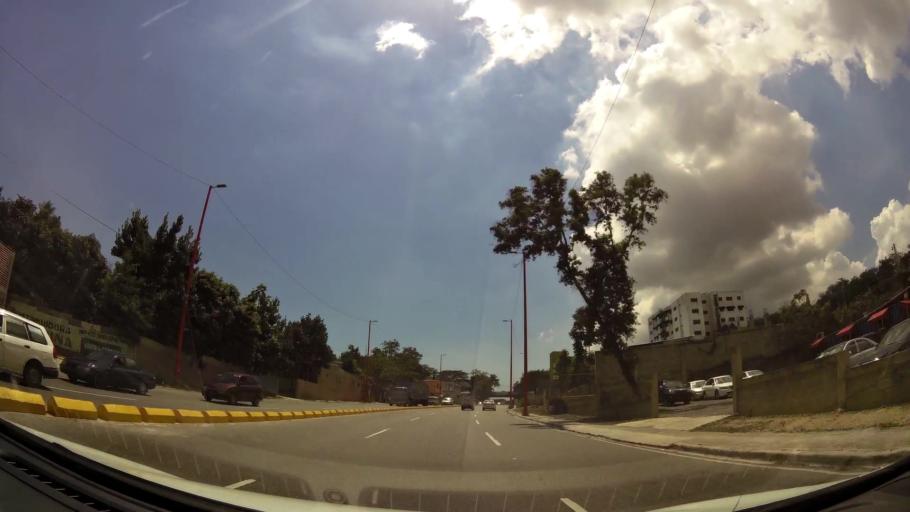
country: DO
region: Nacional
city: La Agustina
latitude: 18.5125
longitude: -69.9558
